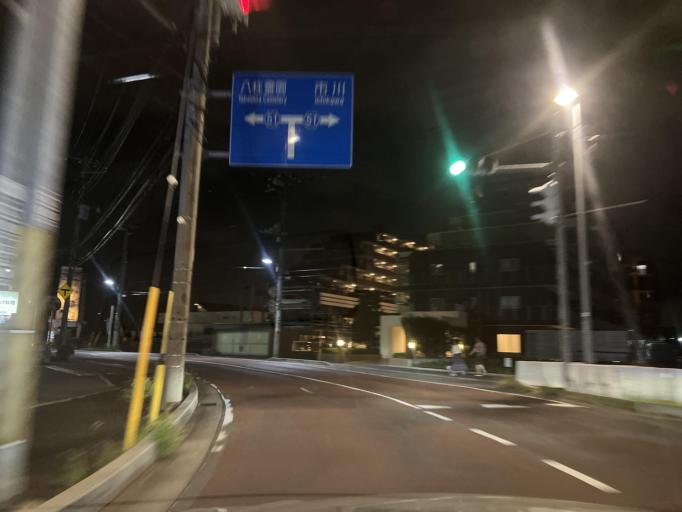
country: JP
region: Chiba
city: Matsudo
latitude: 35.7814
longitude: 139.9418
